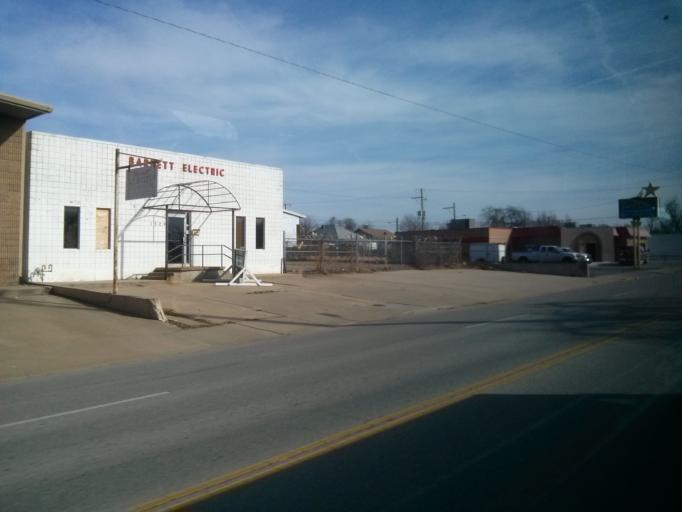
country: US
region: Oklahoma
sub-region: Tulsa County
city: Tulsa
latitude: 36.1566
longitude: -95.9704
